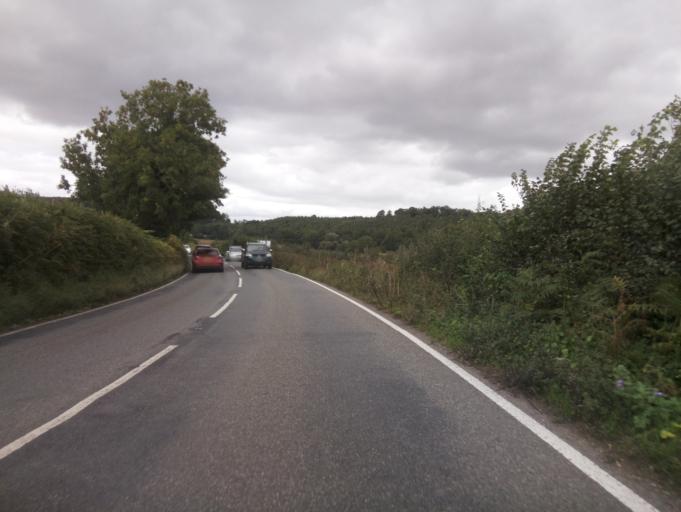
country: GB
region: England
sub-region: Devon
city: Starcross
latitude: 50.6449
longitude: -3.4771
